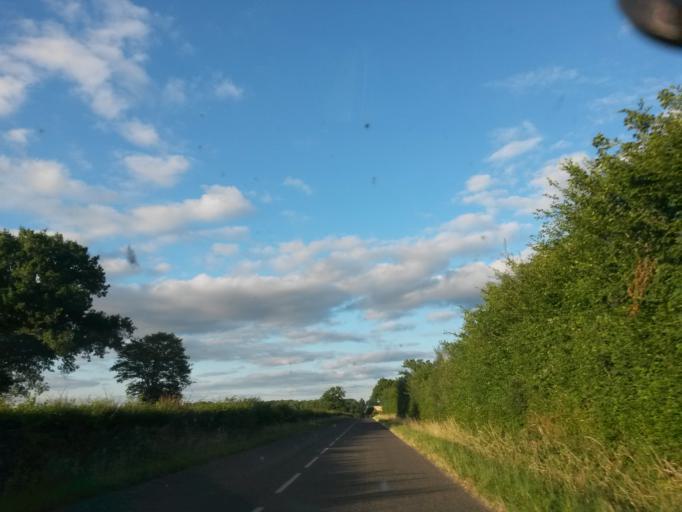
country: FR
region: Bourgogne
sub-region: Departement de la Nievre
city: Corbigny
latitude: 47.2173
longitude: 3.5150
